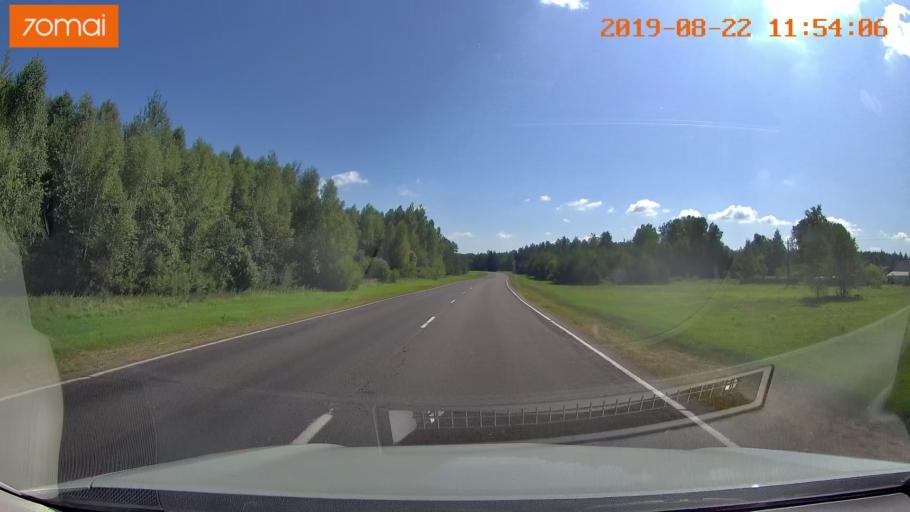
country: BY
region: Minsk
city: Uzda
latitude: 53.4355
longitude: 27.5164
